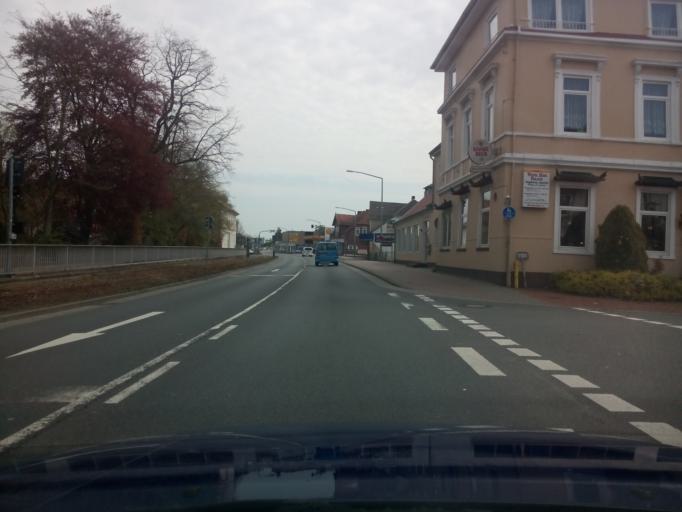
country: DE
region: Lower Saxony
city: Syke
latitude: 52.9129
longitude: 8.8270
